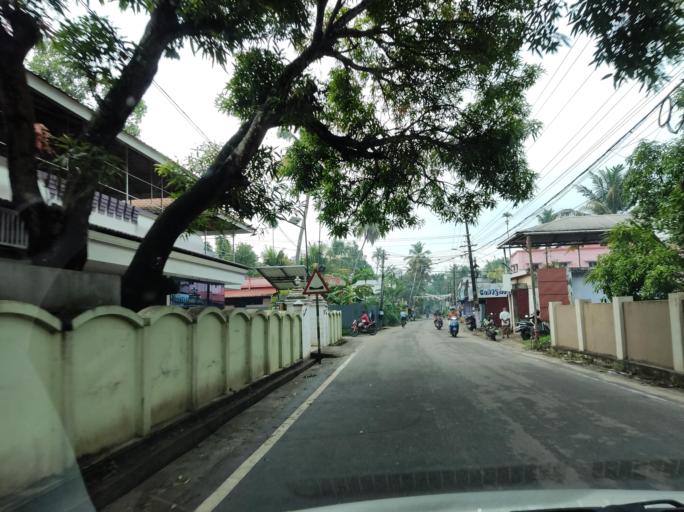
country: IN
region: Kerala
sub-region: Alappuzha
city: Kayankulam
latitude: 9.2183
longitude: 76.4612
